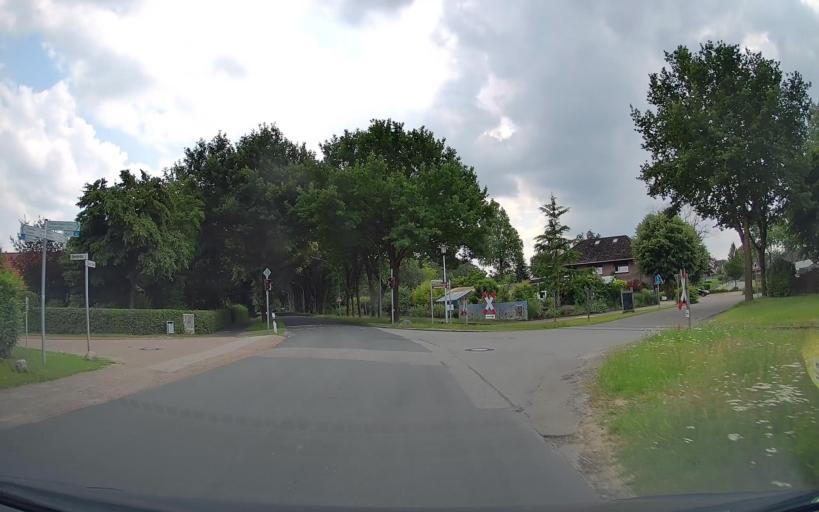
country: DE
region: Lower Saxony
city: Bosel
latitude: 52.9997
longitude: 7.9479
